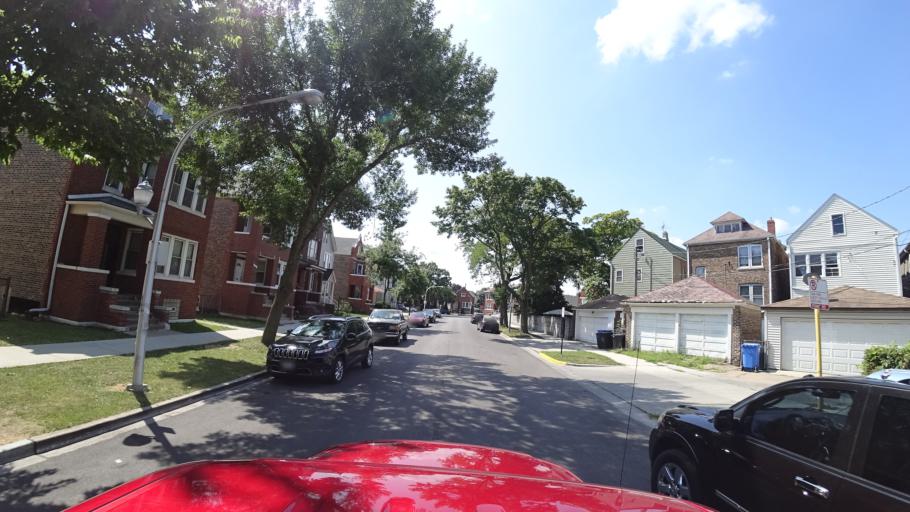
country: US
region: Illinois
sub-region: Cook County
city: Chicago
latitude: 41.8205
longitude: -87.6908
